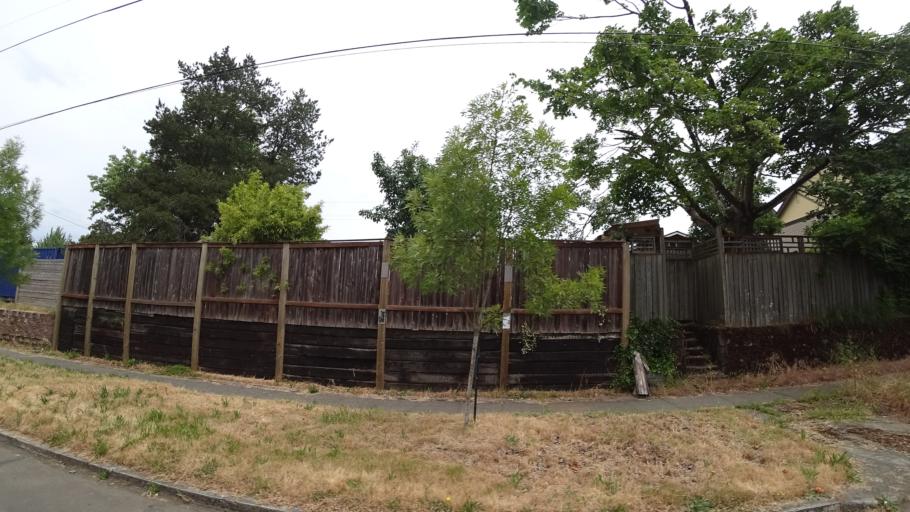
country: US
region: Oregon
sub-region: Multnomah County
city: Portland
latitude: 45.5721
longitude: -122.6983
